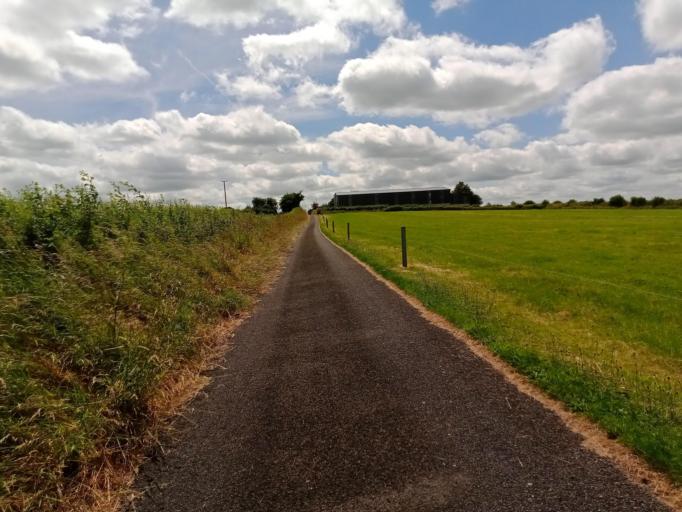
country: IE
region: Leinster
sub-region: Kilkenny
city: Callan
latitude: 52.5487
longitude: -7.4181
